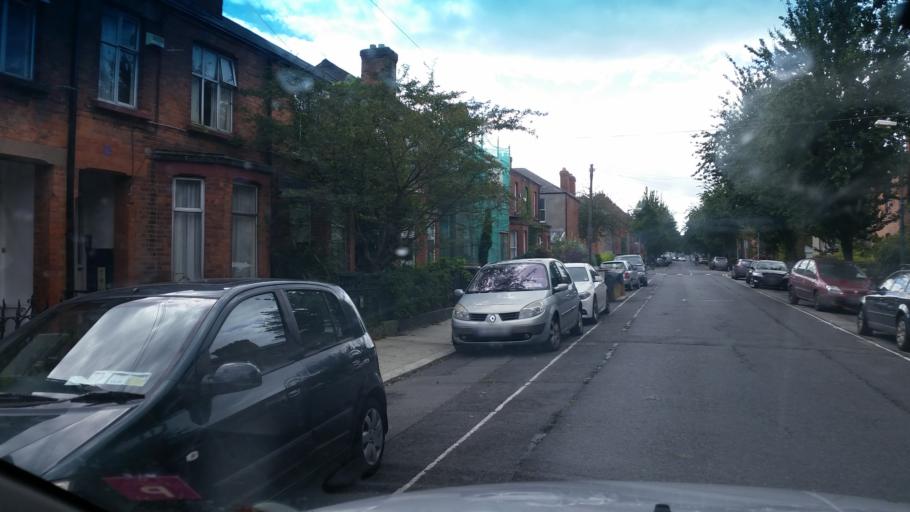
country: IE
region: Leinster
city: Rialto
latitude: 53.3334
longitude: -6.2794
